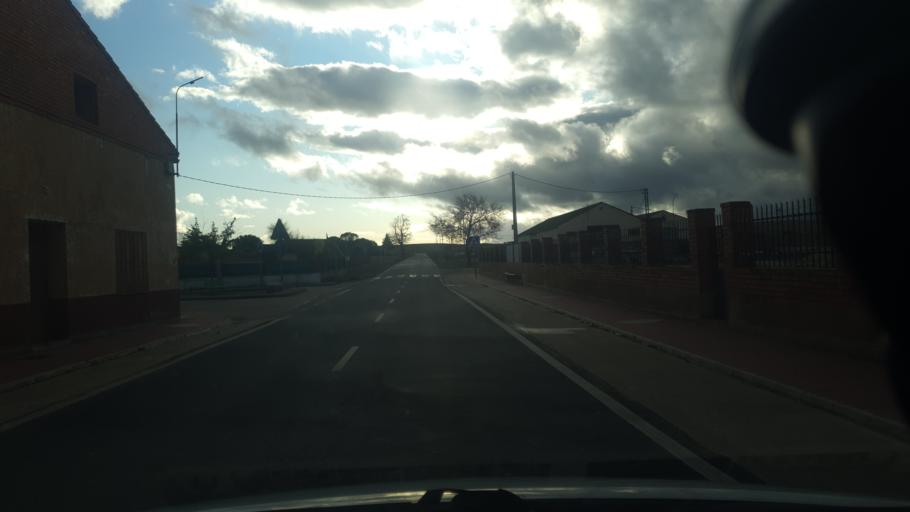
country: ES
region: Castille and Leon
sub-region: Provincia de Segovia
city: Santiuste de San Juan Bautista
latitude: 41.1542
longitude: -4.5725
